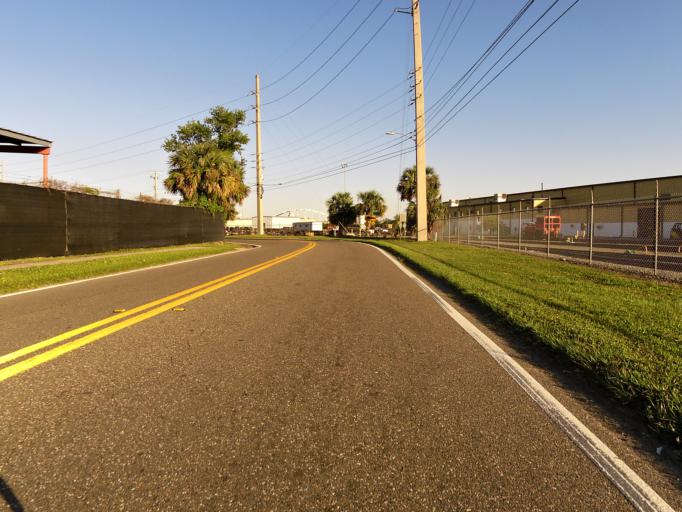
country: US
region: Florida
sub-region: Duval County
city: Jacksonville
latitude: 30.3338
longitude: -81.6817
